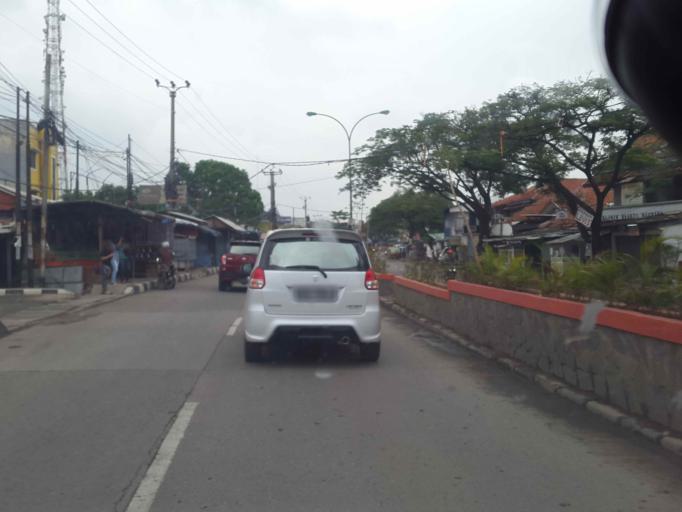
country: ID
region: West Java
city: Cikarang
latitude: -6.2925
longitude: 107.1500
